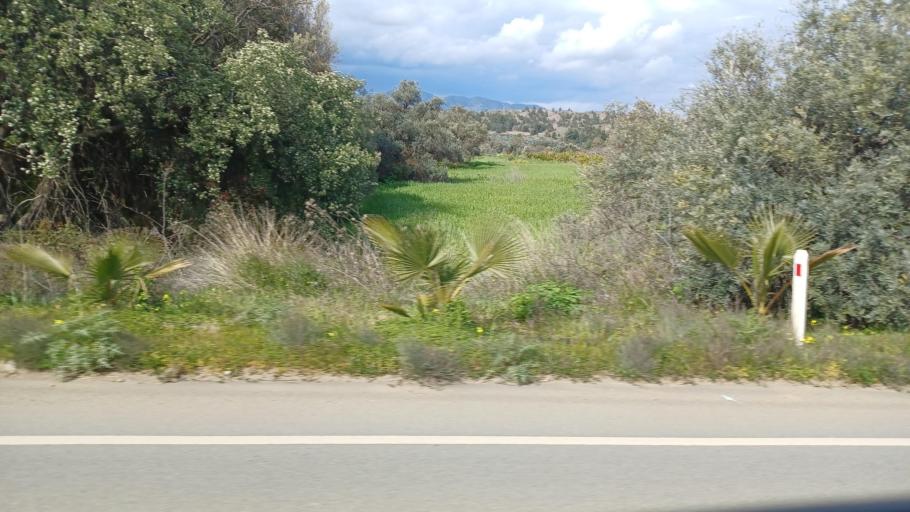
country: CY
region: Lefkosia
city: Lefka
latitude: 35.0862
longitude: 32.8896
